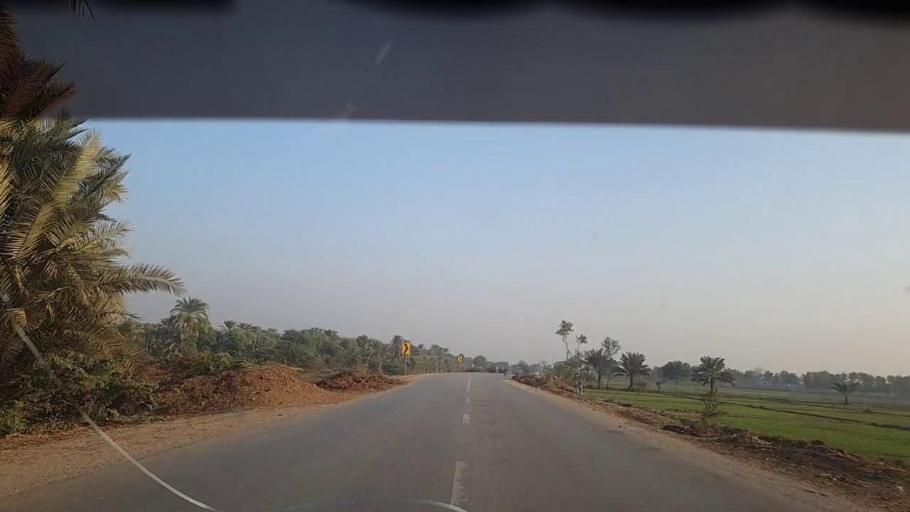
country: PK
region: Sindh
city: Ranipur
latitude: 27.2596
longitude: 68.5272
